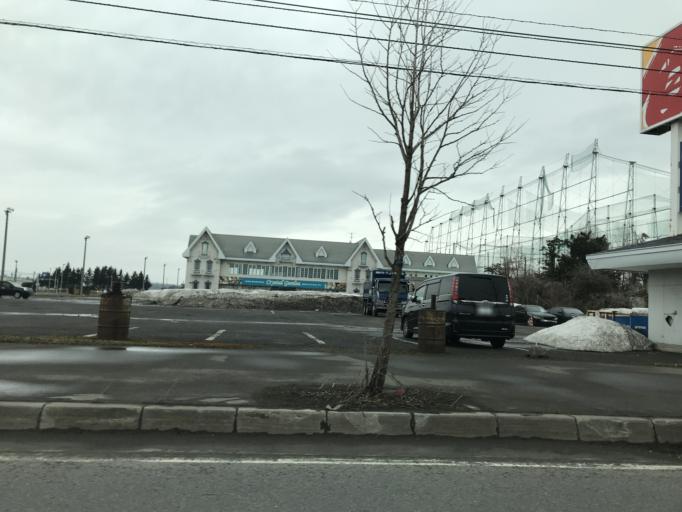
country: JP
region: Hokkaido
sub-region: Asahikawa-shi
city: Asahikawa
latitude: 43.8228
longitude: 142.4133
